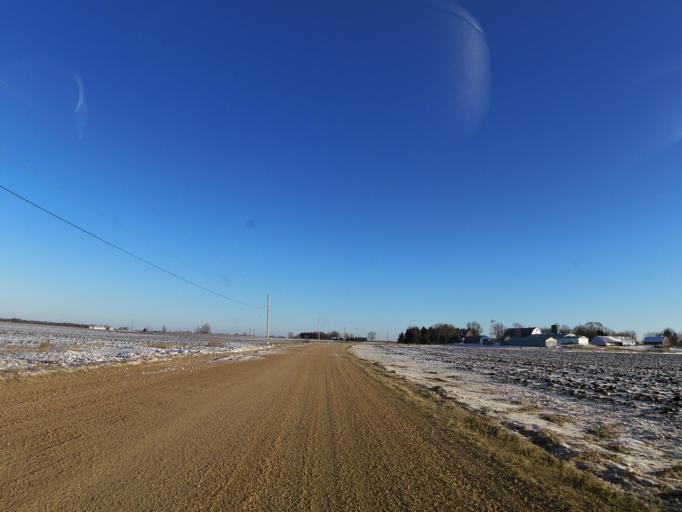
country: US
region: Minnesota
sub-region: Scott County
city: Jordan
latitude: 44.6777
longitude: -93.5361
